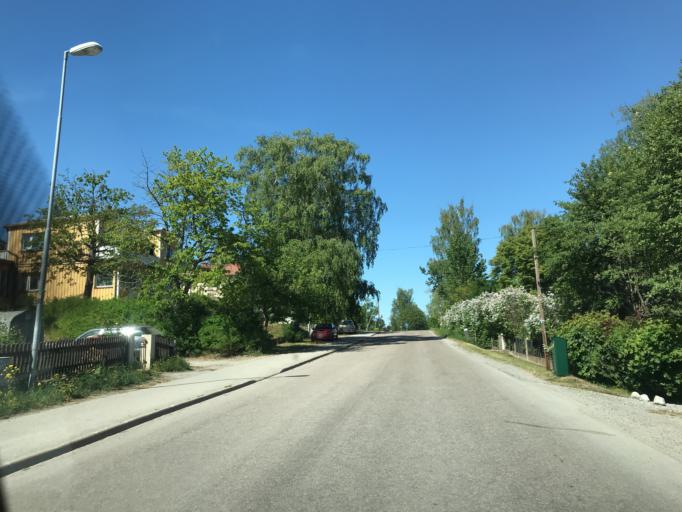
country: SE
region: Stockholm
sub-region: Sollentuna Kommun
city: Sollentuna
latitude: 59.4150
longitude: 17.9728
